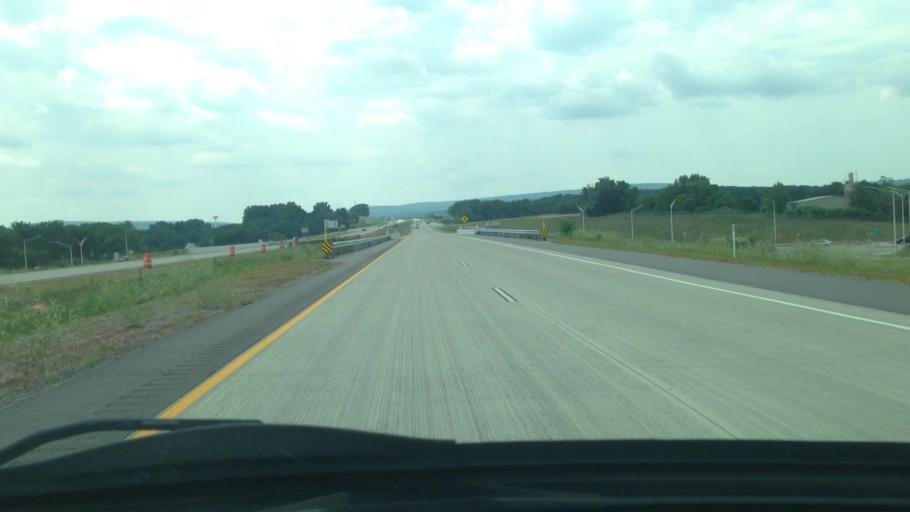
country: US
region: Wisconsin
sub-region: Sauk County
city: West Baraboo
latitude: 43.4764
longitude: -89.7749
